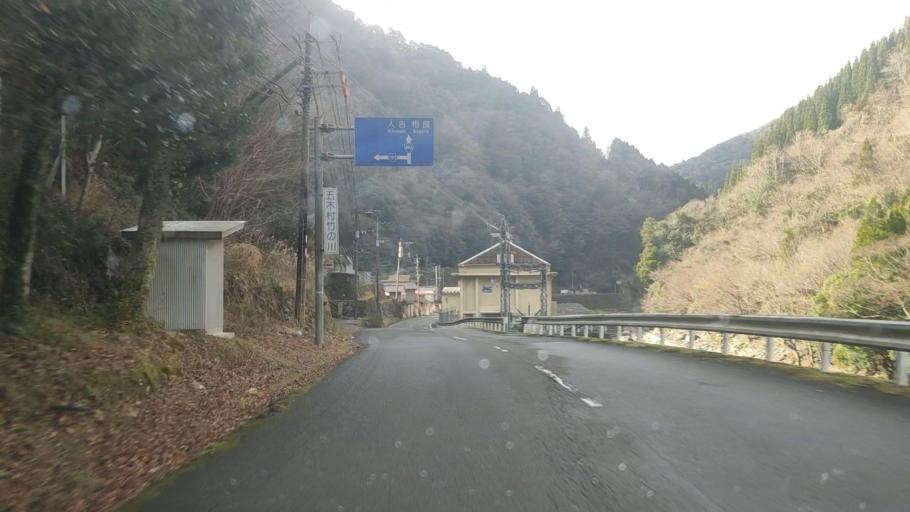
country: JP
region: Kumamoto
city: Hitoyoshi
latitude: 32.4203
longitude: 130.8546
